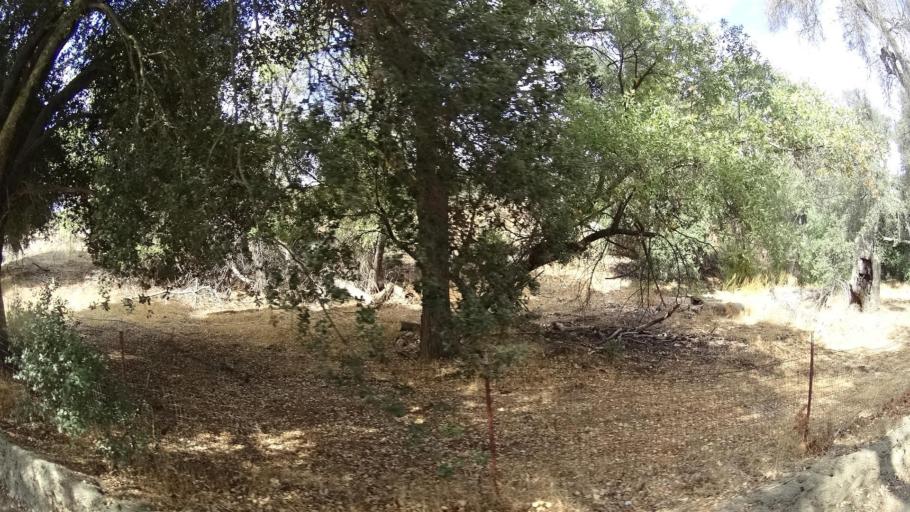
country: US
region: California
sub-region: San Diego County
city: Campo
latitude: 32.6771
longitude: -116.3327
